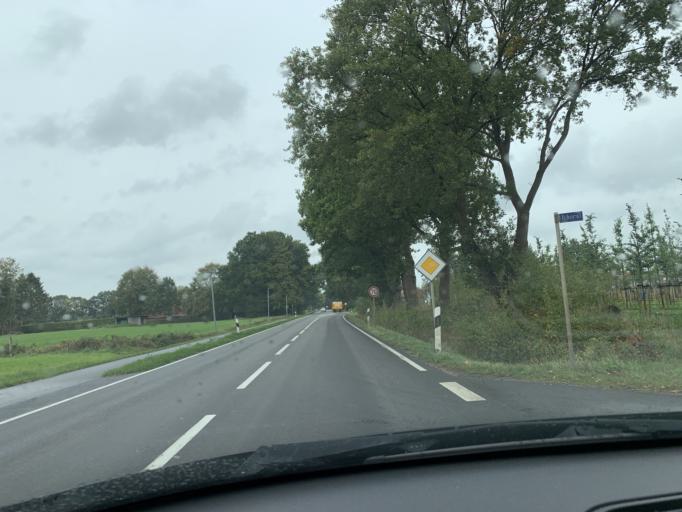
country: DE
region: Lower Saxony
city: Bad Zwischenahn
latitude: 53.1786
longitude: 8.0689
